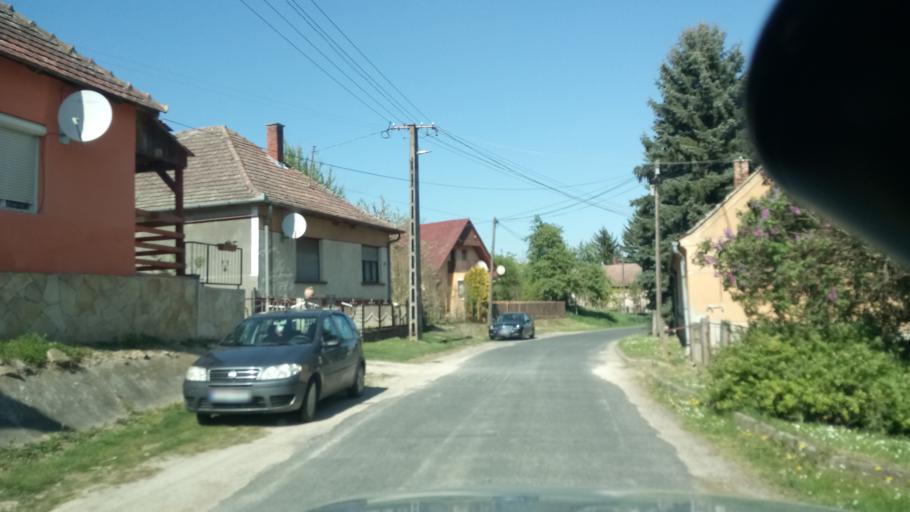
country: HU
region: Zala
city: Sarmellek
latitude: 46.7015
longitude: 17.1045
